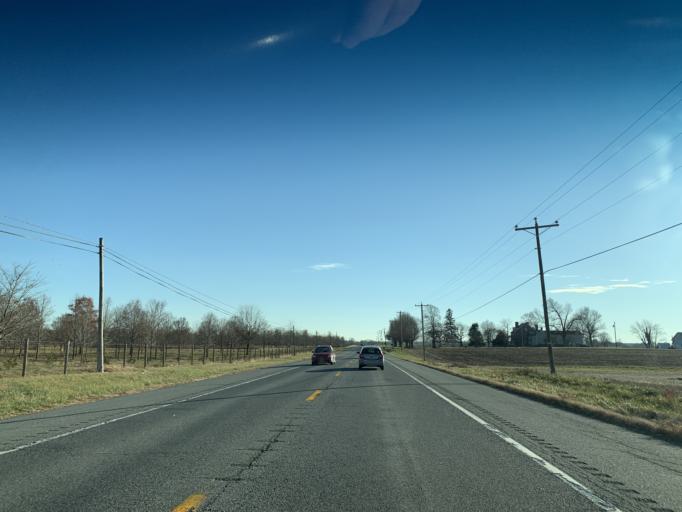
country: US
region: Delaware
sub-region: New Castle County
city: Middletown
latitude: 39.4254
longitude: -75.8605
